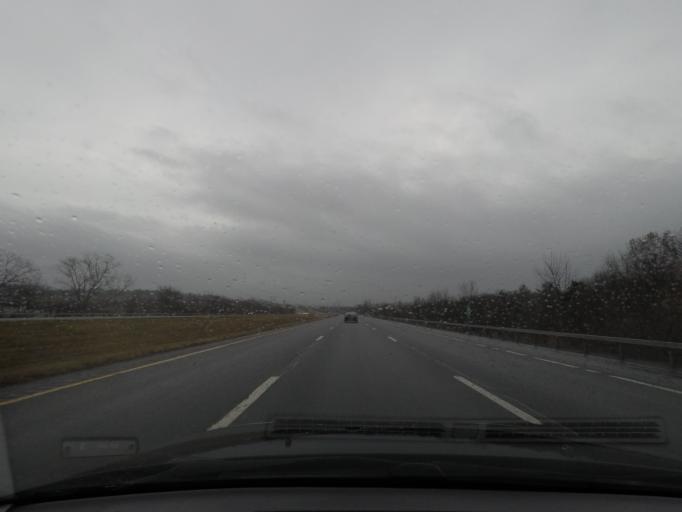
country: US
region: New York
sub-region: Rensselaer County
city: Hampton Manor
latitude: 42.6422
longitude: -73.7102
